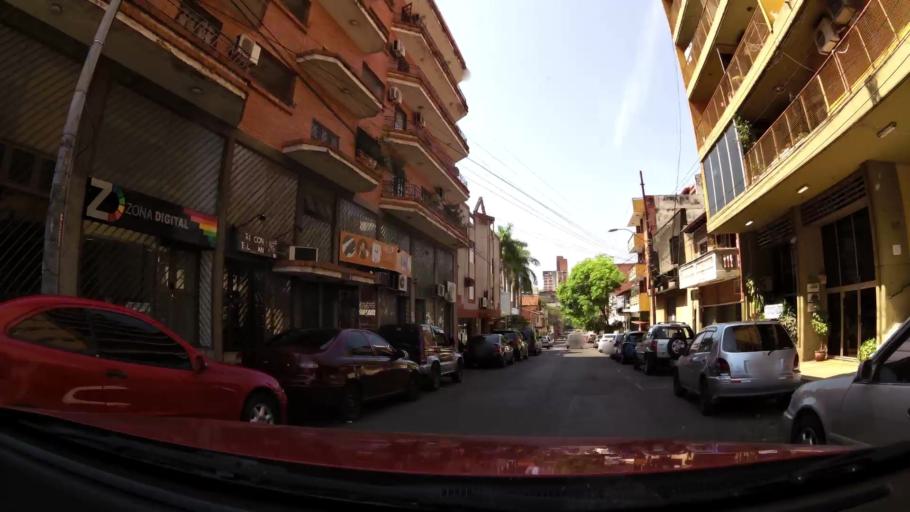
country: PY
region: Asuncion
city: Asuncion
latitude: -25.2858
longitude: -57.6426
